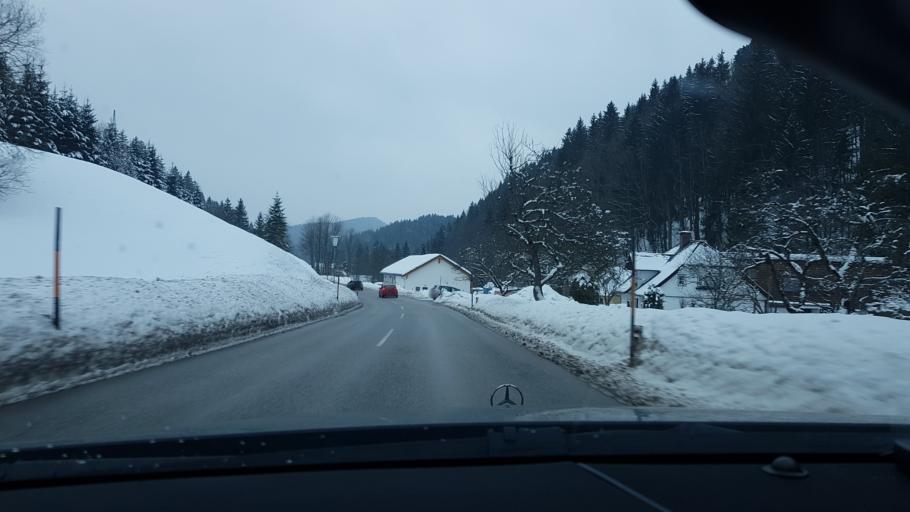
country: AT
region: Lower Austria
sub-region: Politischer Bezirk Scheibbs
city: Gaming
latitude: 47.8715
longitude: 15.1413
